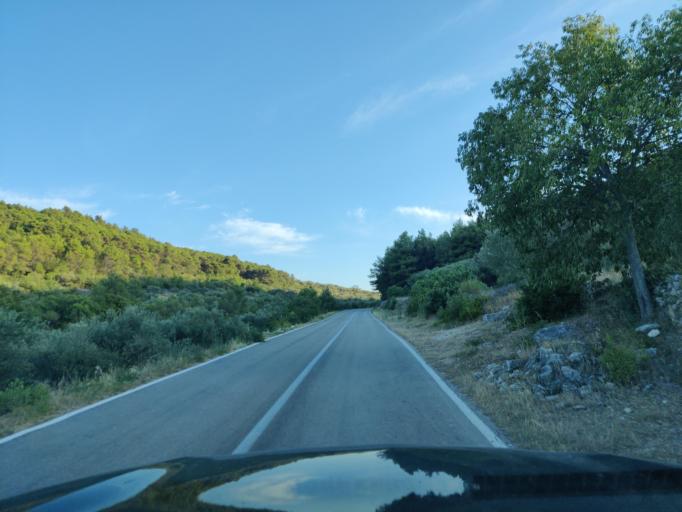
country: HR
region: Sibensko-Kniniska
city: Tribunj
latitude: 43.7917
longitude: 15.7299
